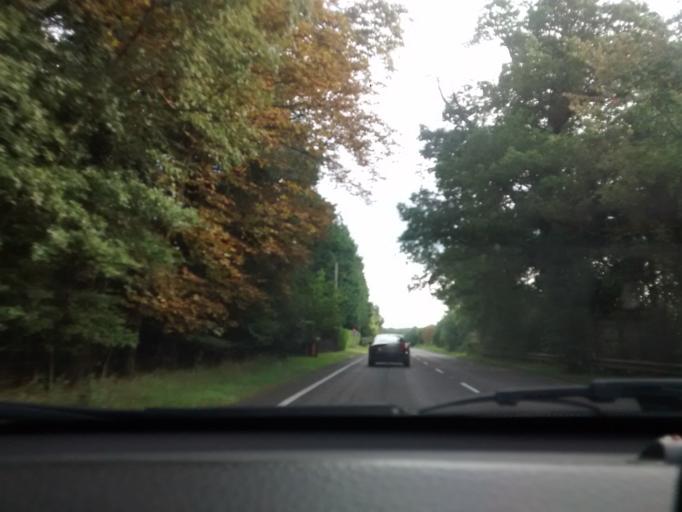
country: GB
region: England
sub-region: Norfolk
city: Downham Market
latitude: 52.5805
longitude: 0.3879
